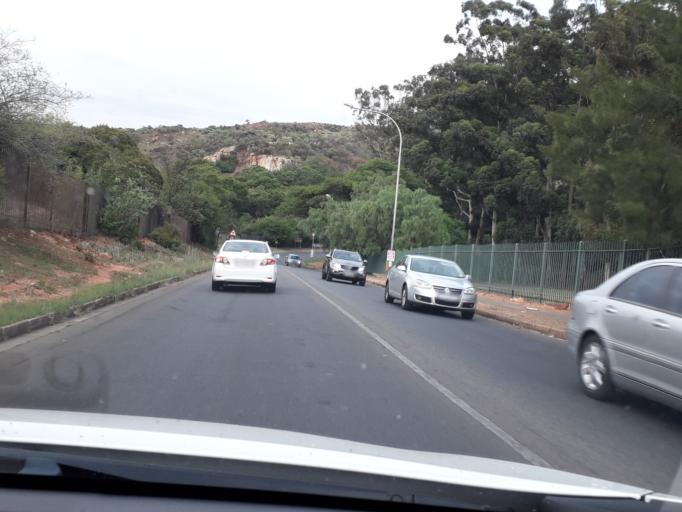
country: ZA
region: Gauteng
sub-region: City of Johannesburg Metropolitan Municipality
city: Johannesburg
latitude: -26.1670
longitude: 28.0004
